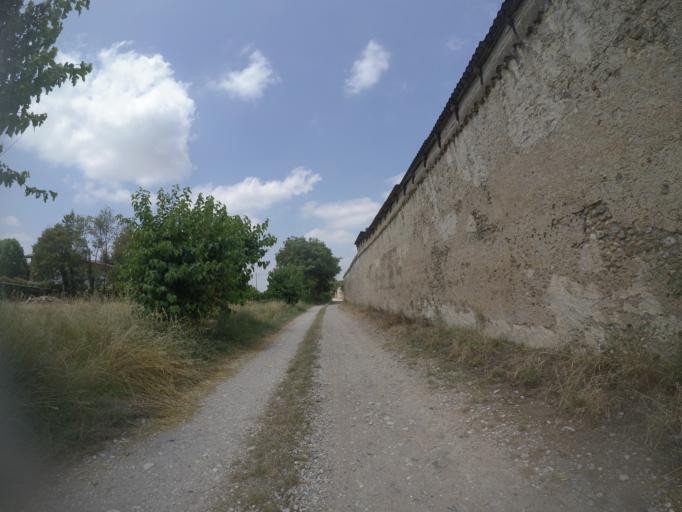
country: IT
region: Friuli Venezia Giulia
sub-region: Provincia di Udine
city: Bertiolo
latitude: 45.9698
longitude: 13.0662
